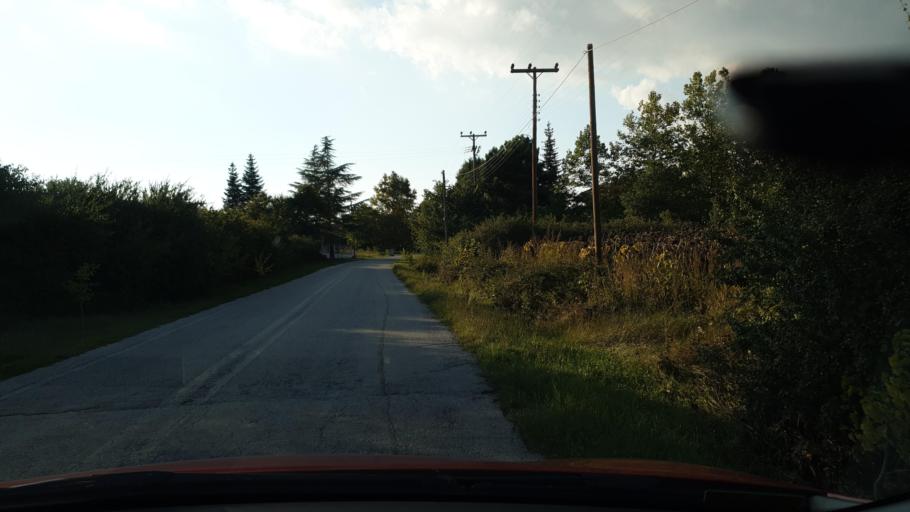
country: GR
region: Central Macedonia
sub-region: Nomos Chalkidikis
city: Galatista
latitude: 40.5191
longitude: 23.2828
